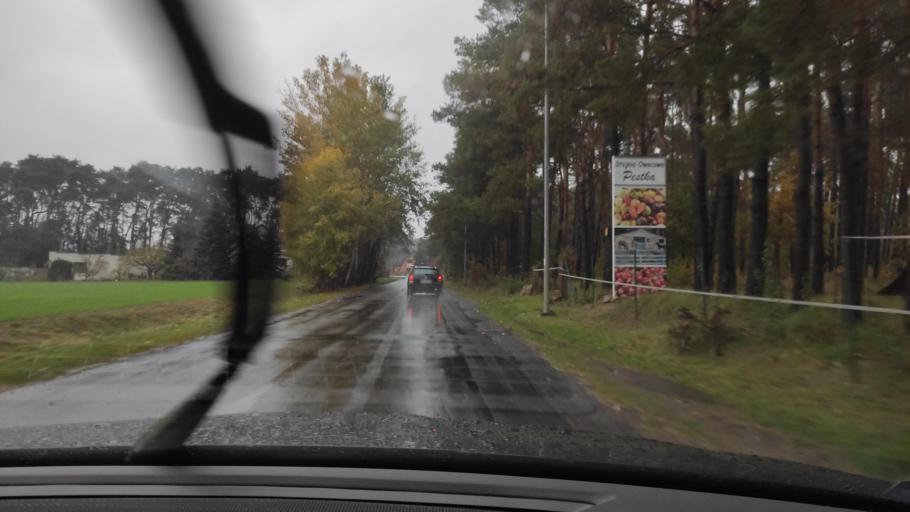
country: PL
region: Greater Poland Voivodeship
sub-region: Powiat poznanski
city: Kornik
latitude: 52.2183
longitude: 17.0985
